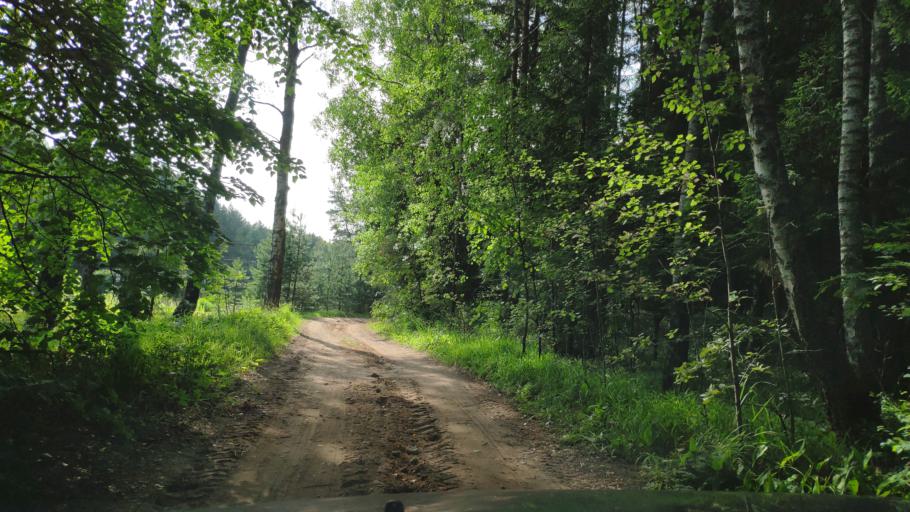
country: BY
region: Minsk
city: Zaslawye
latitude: 53.9679
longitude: 27.2957
